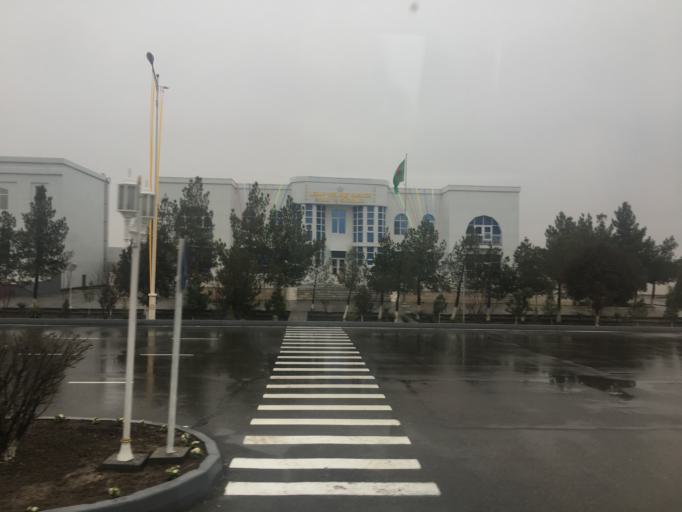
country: TM
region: Lebap
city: Turkmenabat
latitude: 39.0683
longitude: 63.5870
